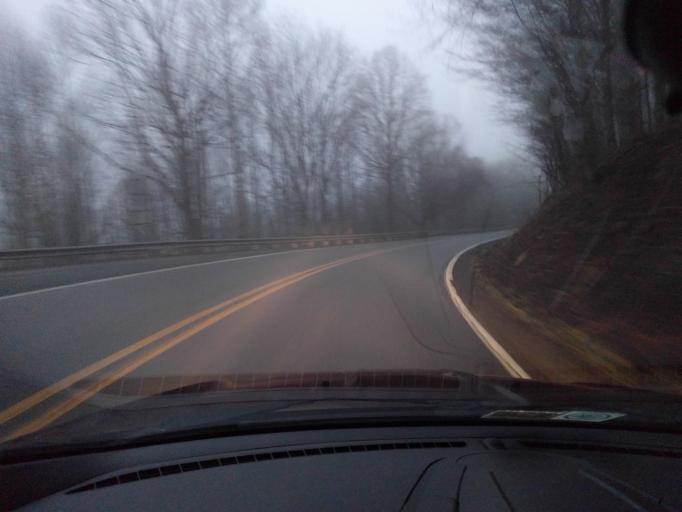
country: US
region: West Virginia
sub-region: Greenbrier County
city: Rainelle
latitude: 37.9735
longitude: -80.8195
